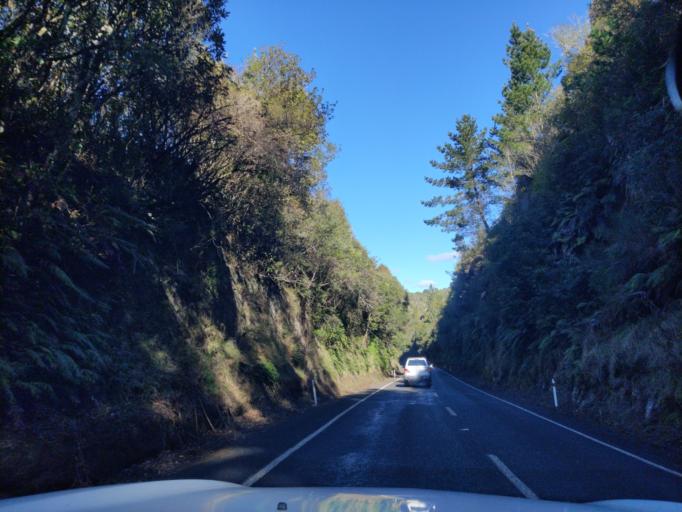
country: NZ
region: Waikato
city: Turangi
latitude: -38.7518
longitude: 175.6765
